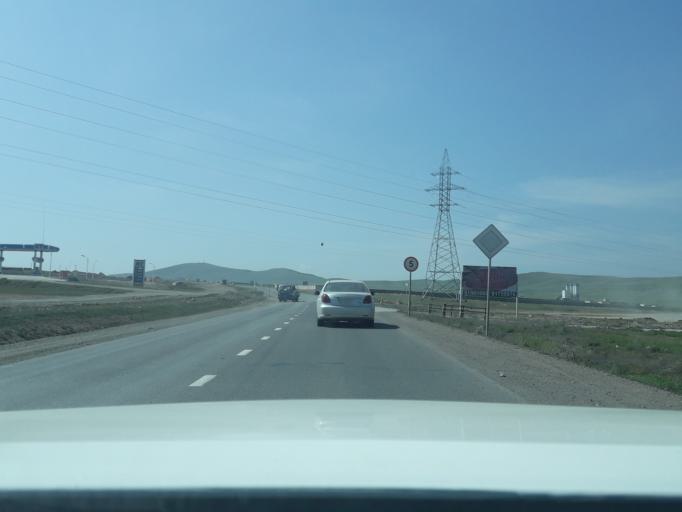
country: MN
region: Ulaanbaatar
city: Ulaanbaatar
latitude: 47.8186
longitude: 106.7584
